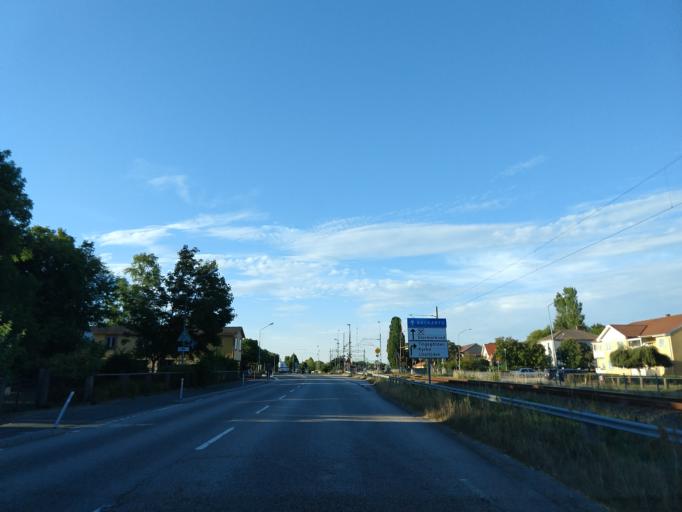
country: SE
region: Blekinge
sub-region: Ronneby Kommun
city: Brakne-Hoby
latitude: 56.2288
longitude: 15.1148
